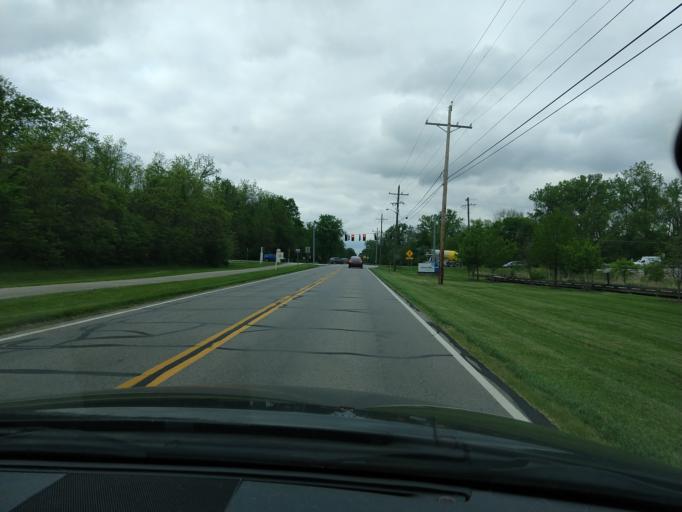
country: US
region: Indiana
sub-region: Hamilton County
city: Westfield
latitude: 40.0211
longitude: -86.1275
